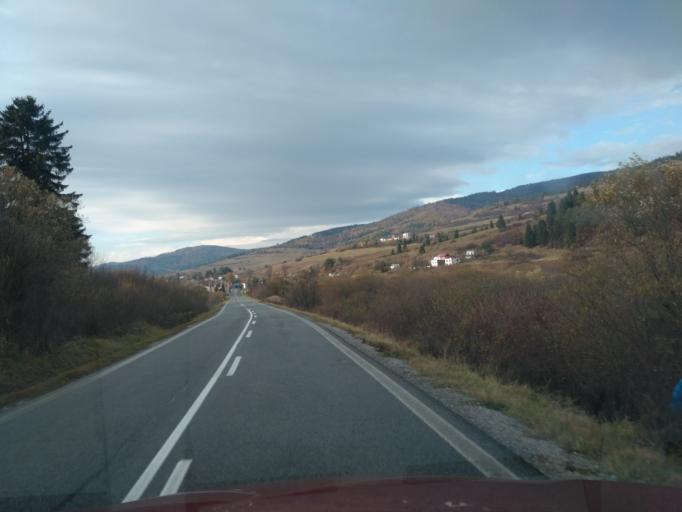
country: SK
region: Kosicky
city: Krompachy
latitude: 48.8035
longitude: 20.7296
